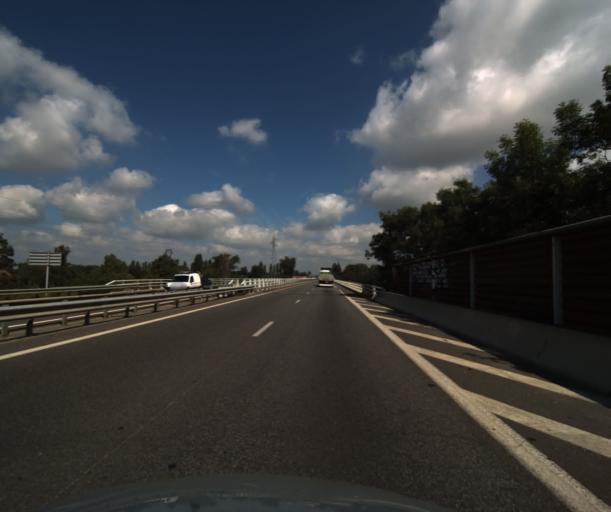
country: FR
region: Midi-Pyrenees
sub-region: Departement de la Haute-Garonne
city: Pinsaguel
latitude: 43.5090
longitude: 1.3832
